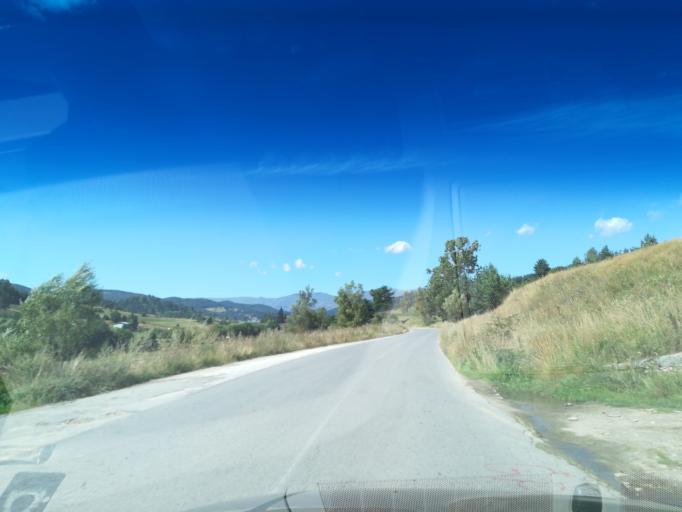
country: BG
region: Sofiya
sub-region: Obshtina Koprivshtitsa
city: Koprivshtitsa
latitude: 42.6086
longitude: 24.3767
